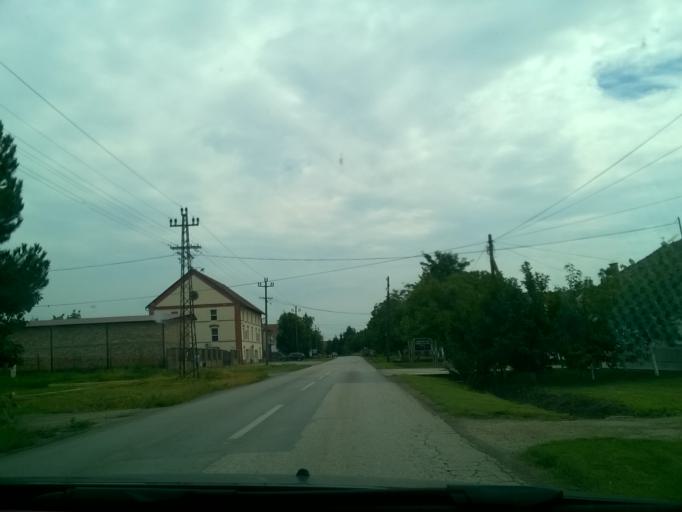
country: RS
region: Autonomna Pokrajina Vojvodina
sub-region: Srednjebanatski Okrug
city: Secanj
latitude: 45.3676
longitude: 20.7648
